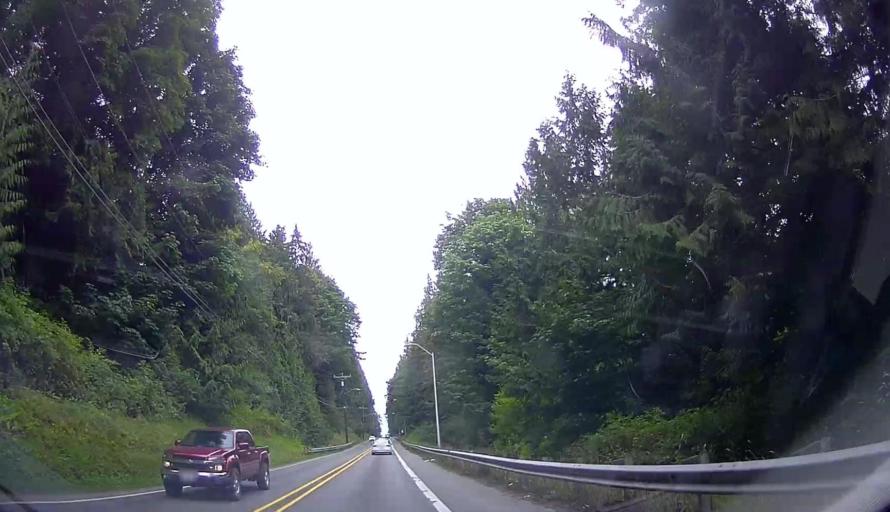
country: US
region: Washington
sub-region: Snohomish County
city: Tulalip
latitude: 48.0426
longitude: -122.2520
